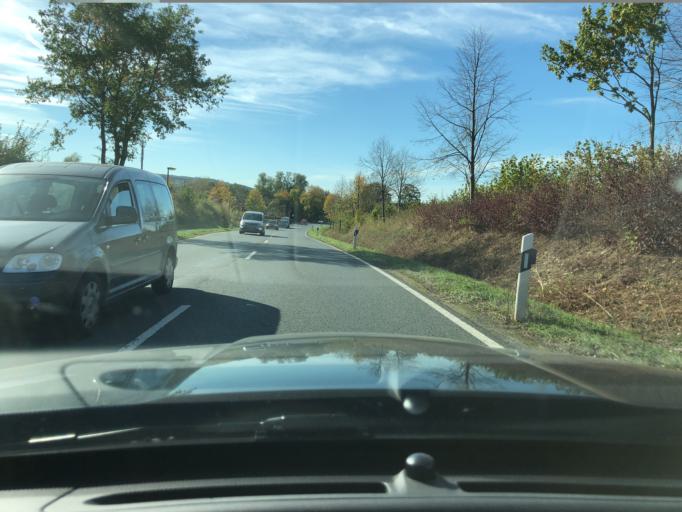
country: DE
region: Lower Saxony
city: Hagen
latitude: 52.2473
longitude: 7.9826
